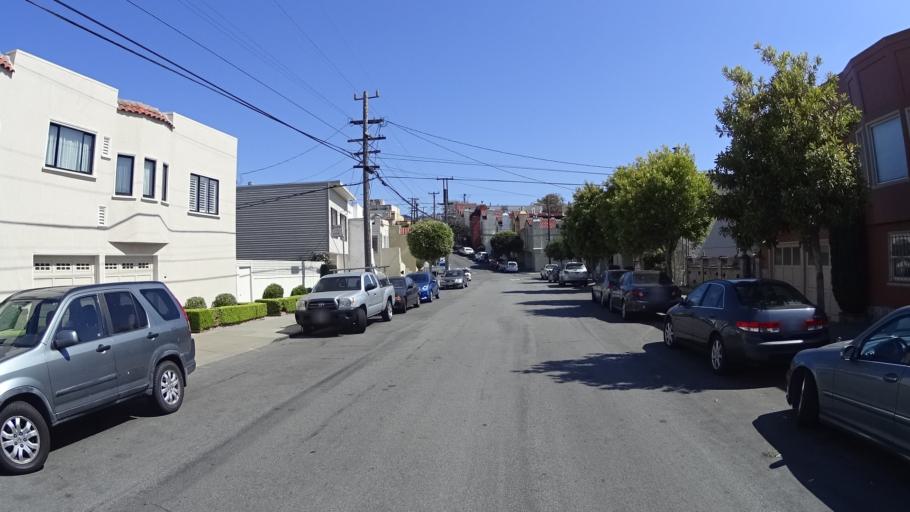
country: US
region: California
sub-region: San Mateo County
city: Daly City
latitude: 37.7254
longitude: -122.4386
